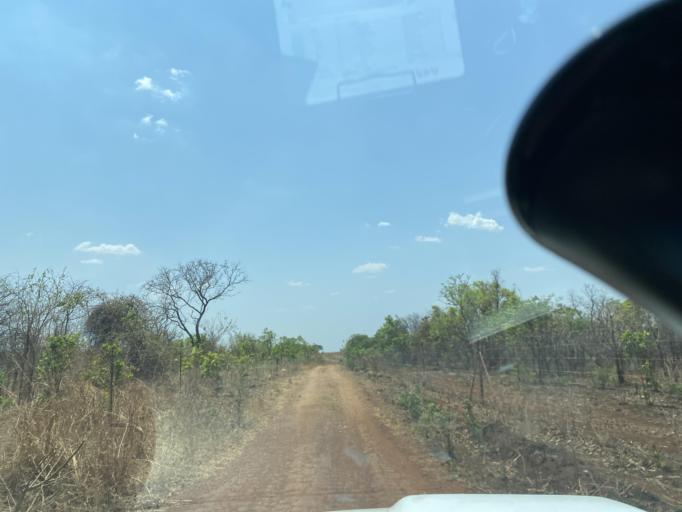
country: ZM
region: Lusaka
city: Lusaka
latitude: -15.5015
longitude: 27.9696
